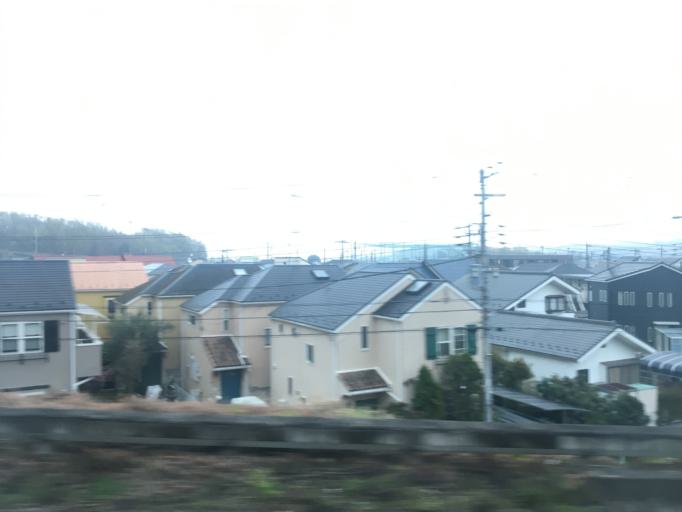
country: JP
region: Tokyo
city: Hino
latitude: 35.6678
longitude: 139.3899
